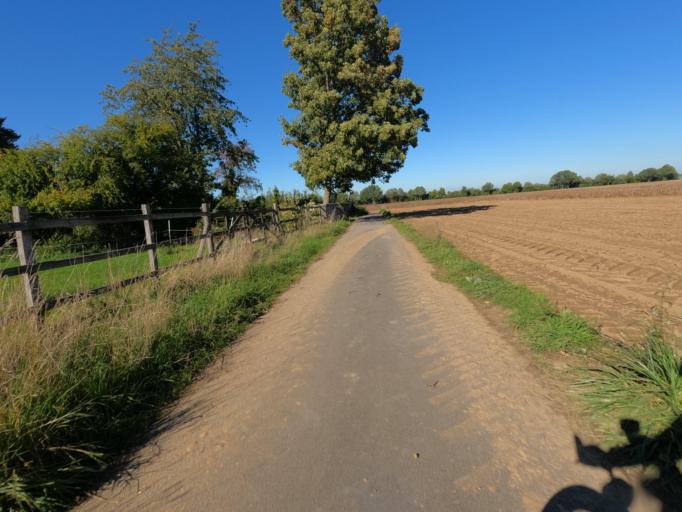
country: DE
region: North Rhine-Westphalia
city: Erkelenz
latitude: 51.0663
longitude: 6.3500
